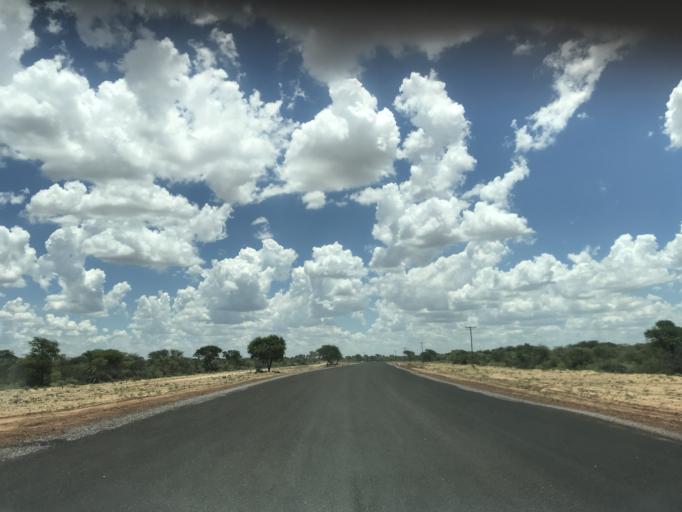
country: BW
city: Mabuli
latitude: -25.8000
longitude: 24.6696
